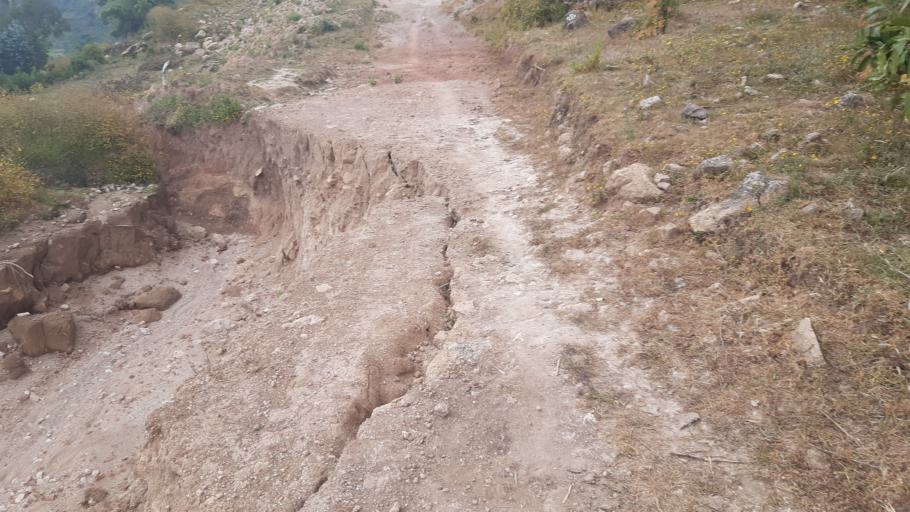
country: ET
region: Amhara
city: Dabat
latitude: 13.3418
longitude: 37.4063
